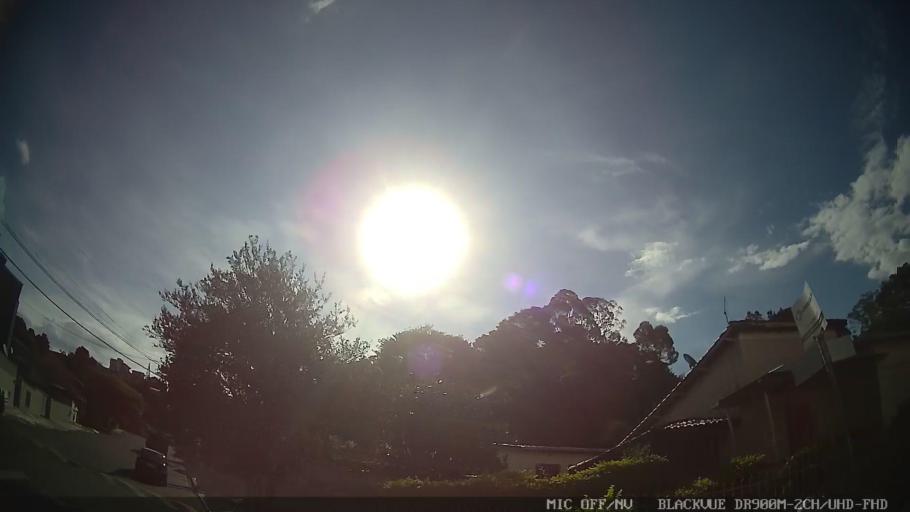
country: BR
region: Sao Paulo
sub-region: Serra Negra
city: Serra Negra
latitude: -22.6189
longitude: -46.7007
